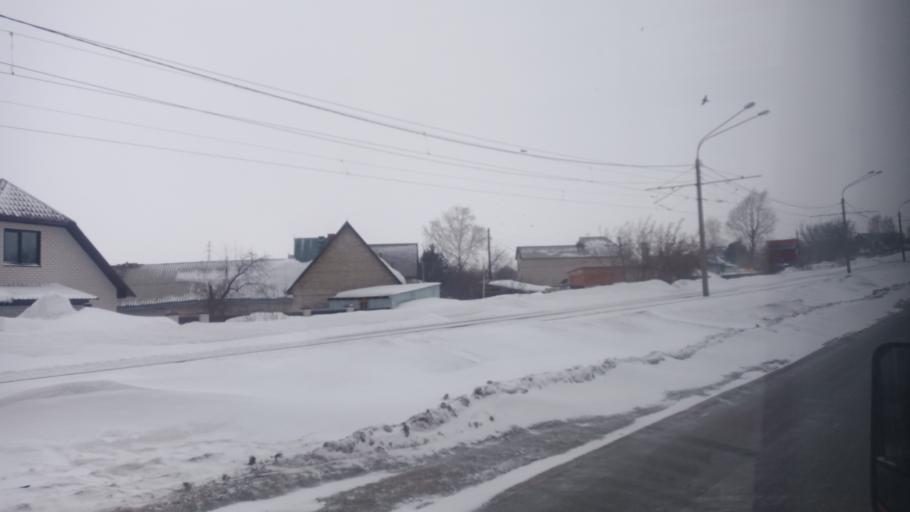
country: RU
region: Altai Krai
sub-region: Gorod Barnaulskiy
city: Barnaul
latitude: 53.3880
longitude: 83.6805
